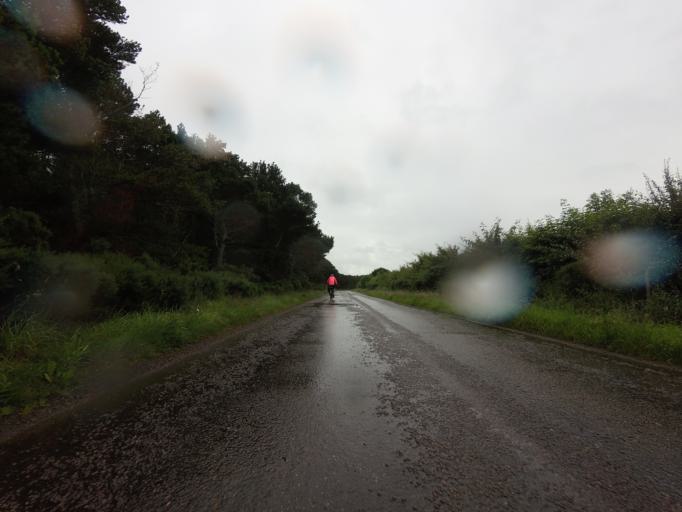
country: GB
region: Scotland
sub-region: Moray
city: Fochabers
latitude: 57.6651
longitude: -3.0746
